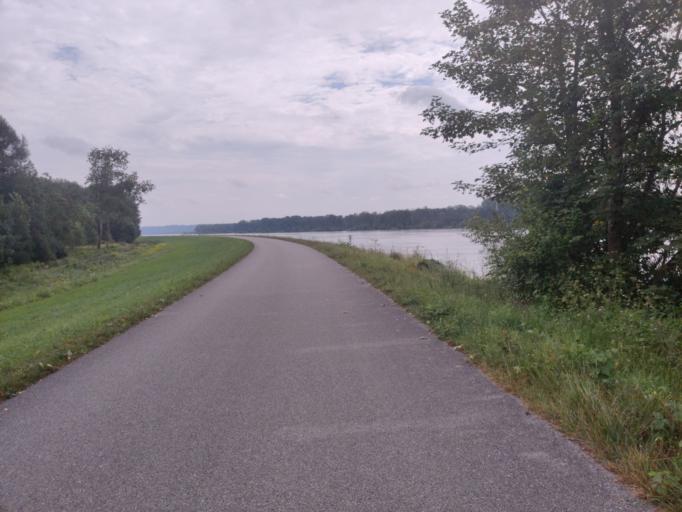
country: AT
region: Upper Austria
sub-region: Politischer Bezirk Perg
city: Perg
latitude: 48.1985
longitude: 14.6112
